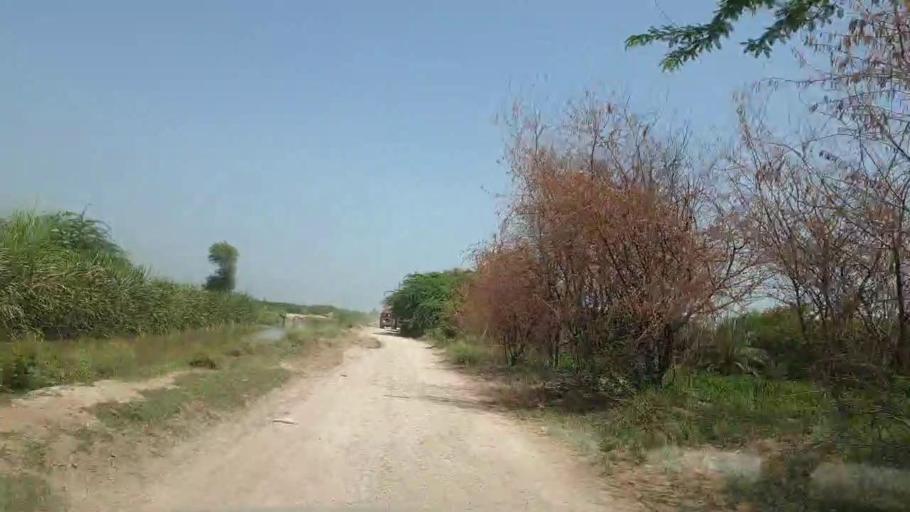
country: PK
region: Sindh
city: Rohri
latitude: 27.6334
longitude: 69.1003
